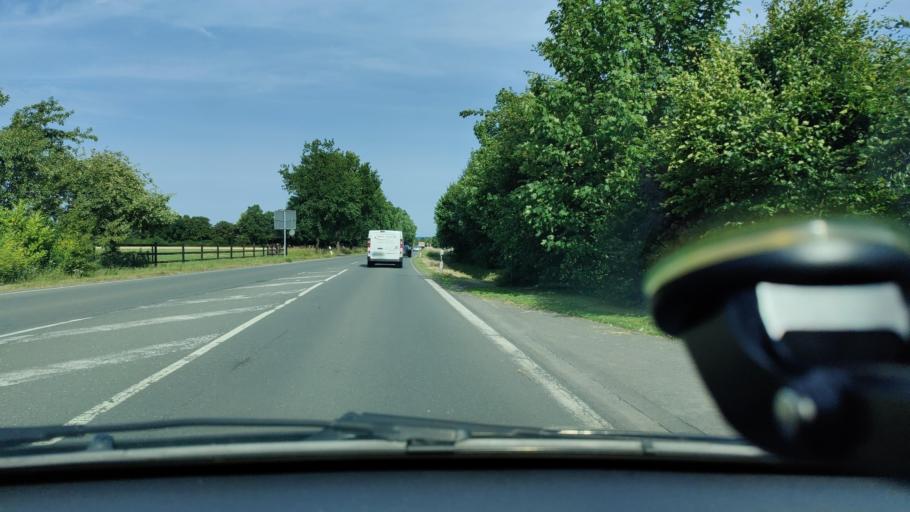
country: DE
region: North Rhine-Westphalia
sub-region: Regierungsbezirk Munster
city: Coesfeld
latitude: 52.0182
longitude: 7.1837
